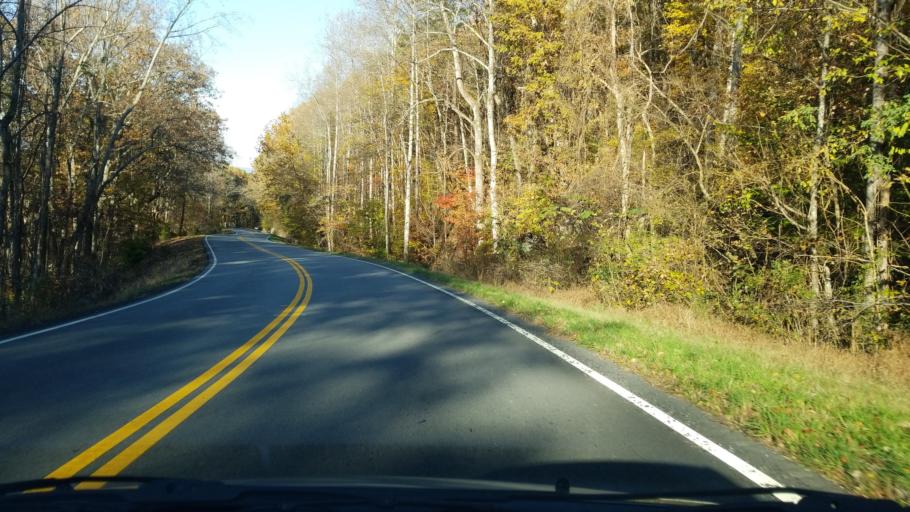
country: US
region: Georgia
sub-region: Dade County
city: Trenton
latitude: 34.8471
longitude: -85.4994
